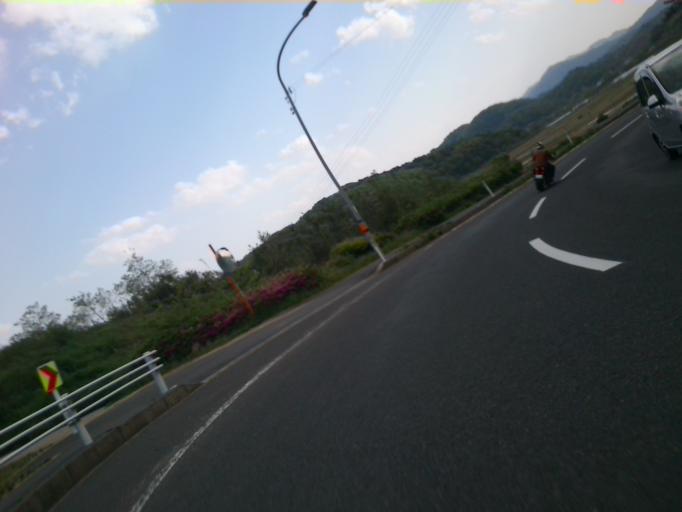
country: JP
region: Kyoto
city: Miyazu
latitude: 35.6941
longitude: 135.0462
